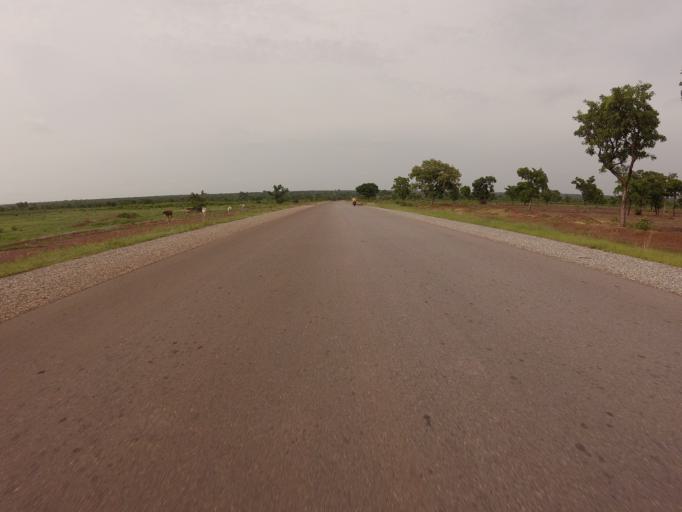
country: GH
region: Northern
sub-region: Yendi
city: Yendi
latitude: 9.8019
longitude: -0.1132
